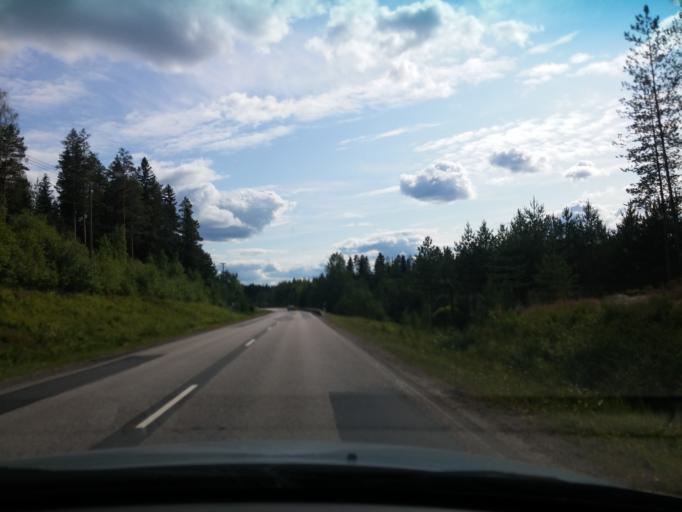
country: FI
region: Central Finland
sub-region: Keuruu
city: Multia
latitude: 62.3550
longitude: 24.7392
